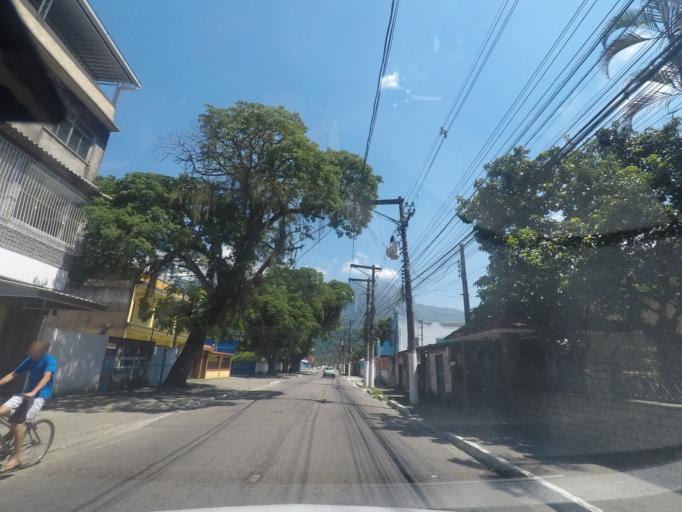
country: BR
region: Rio de Janeiro
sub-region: Petropolis
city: Petropolis
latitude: -22.5839
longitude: -43.1865
